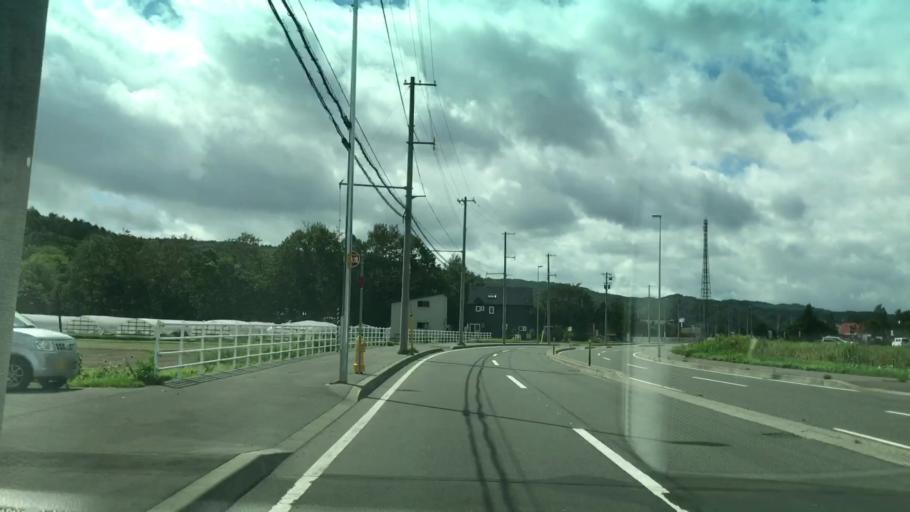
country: JP
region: Hokkaido
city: Kitahiroshima
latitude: 42.9564
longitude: 141.4542
